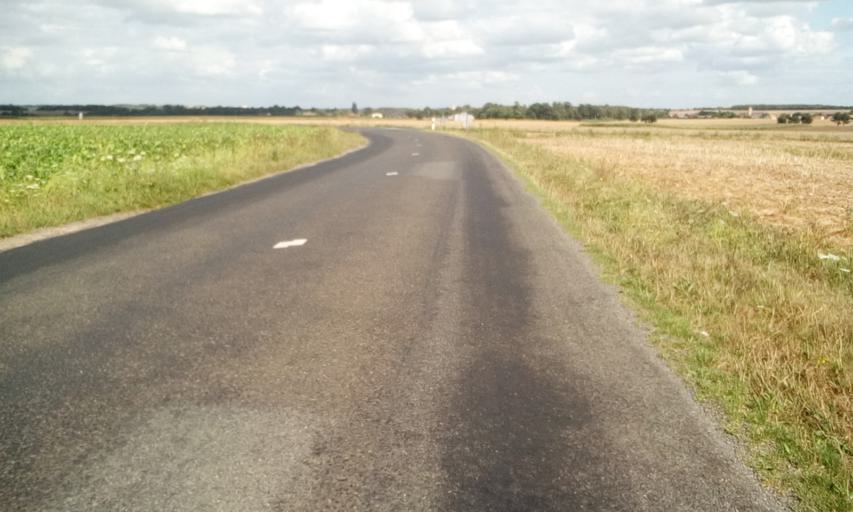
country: FR
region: Lower Normandy
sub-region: Departement du Calvados
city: Bellengreville
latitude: 49.0933
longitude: -0.2124
